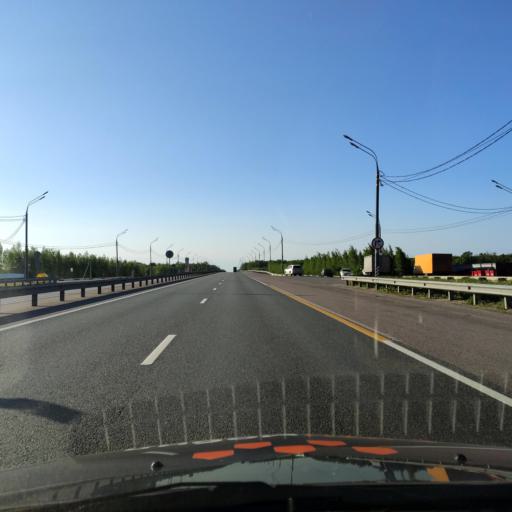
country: RU
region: Lipetsk
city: Zadonsk
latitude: 52.4268
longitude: 38.8289
